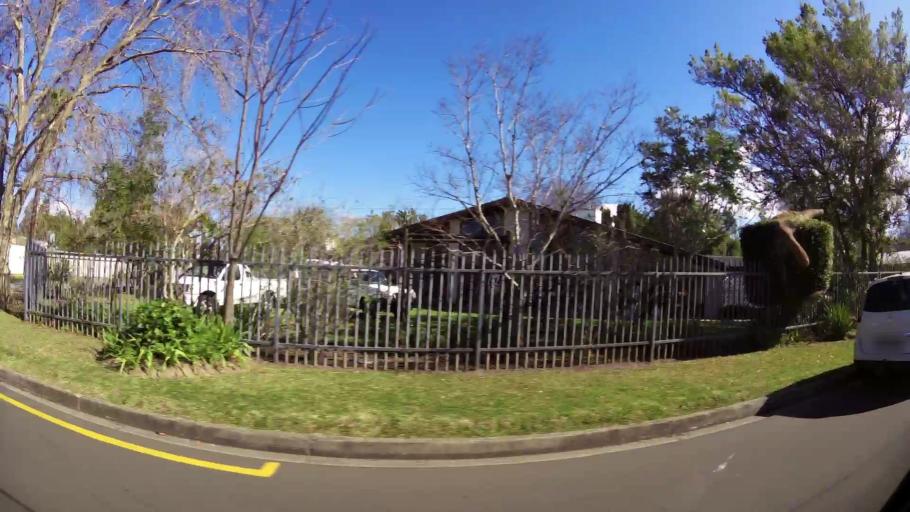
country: ZA
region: Western Cape
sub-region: Eden District Municipality
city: George
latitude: -33.9509
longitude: 22.4408
